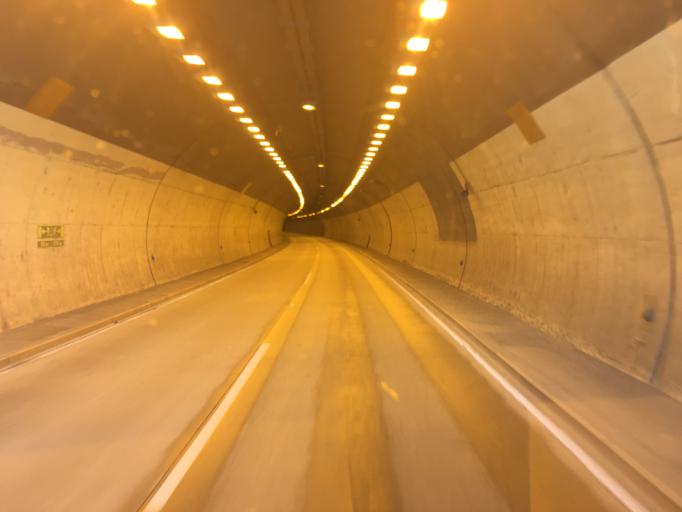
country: CZ
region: Ustecky
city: Libouchec
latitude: 50.7438
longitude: 14.0084
